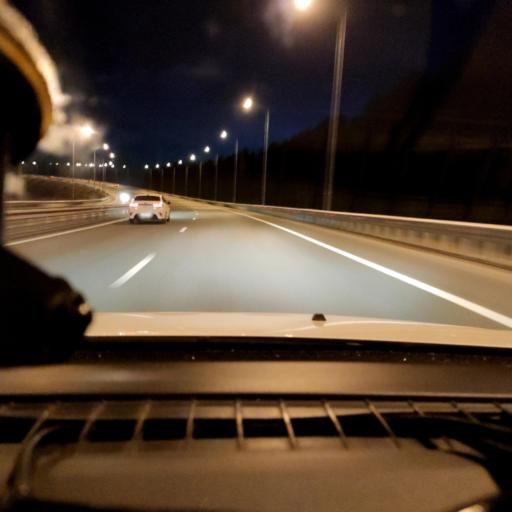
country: RU
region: Samara
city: Bereza
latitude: 53.5057
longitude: 50.1234
